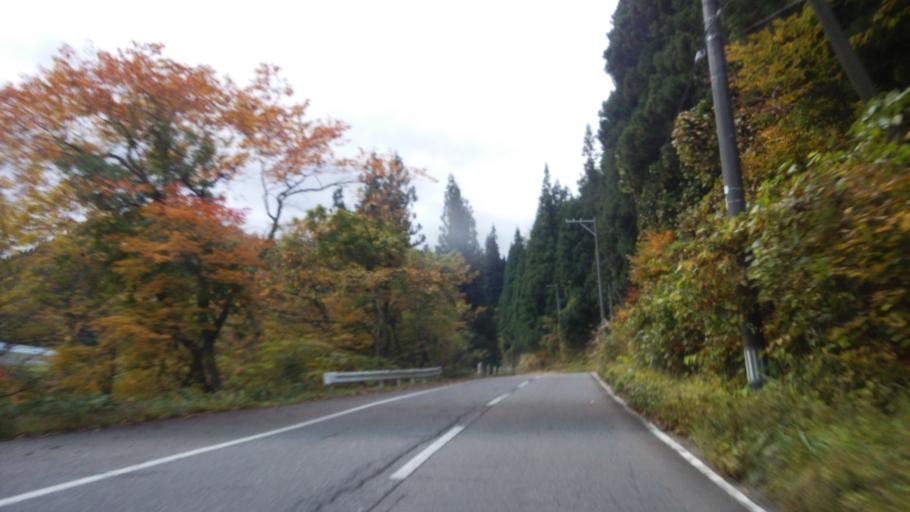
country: JP
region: Fukushima
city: Kitakata
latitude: 37.4126
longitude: 139.6998
